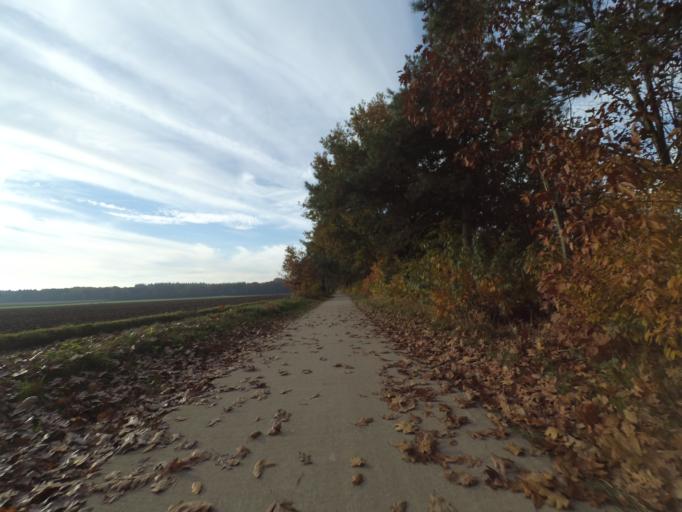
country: NL
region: Gelderland
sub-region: Gemeente Renkum
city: Renkum
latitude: 52.0178
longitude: 5.7241
